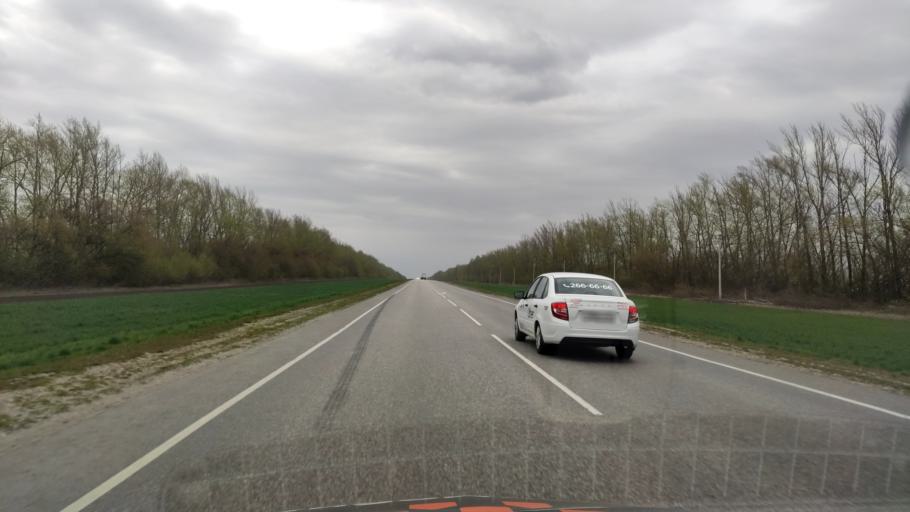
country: RU
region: Kursk
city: Gorshechnoye
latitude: 51.5496
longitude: 38.1617
